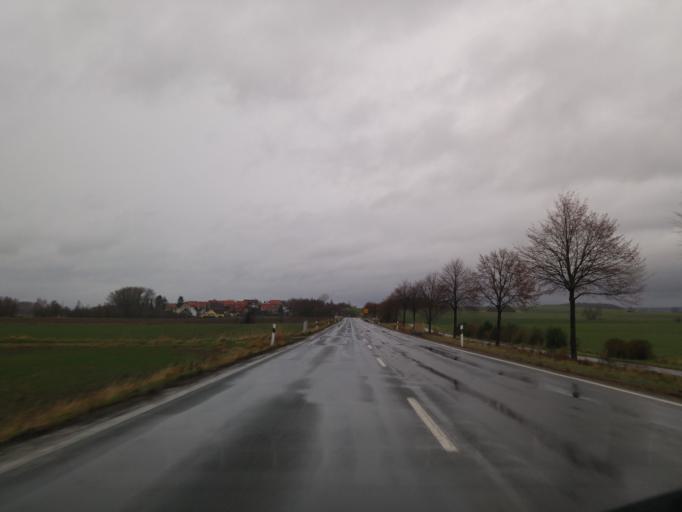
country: DE
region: Lower Saxony
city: Gemeinde Friedland
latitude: 51.4517
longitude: 9.9328
